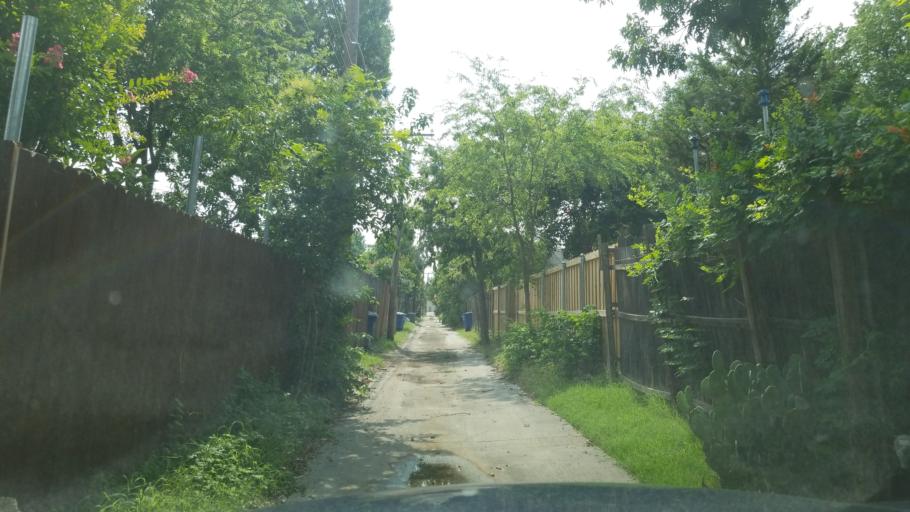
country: US
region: Texas
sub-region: Dallas County
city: Farmers Branch
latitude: 32.9000
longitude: -96.8784
